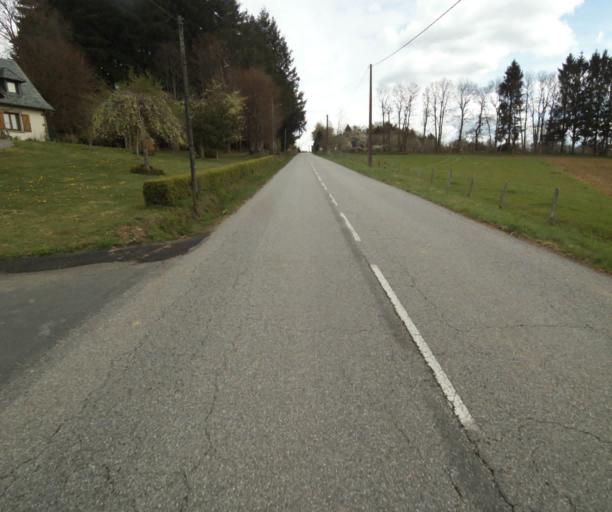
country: FR
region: Limousin
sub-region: Departement de la Correze
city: Laguenne
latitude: 45.2101
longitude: 1.8733
